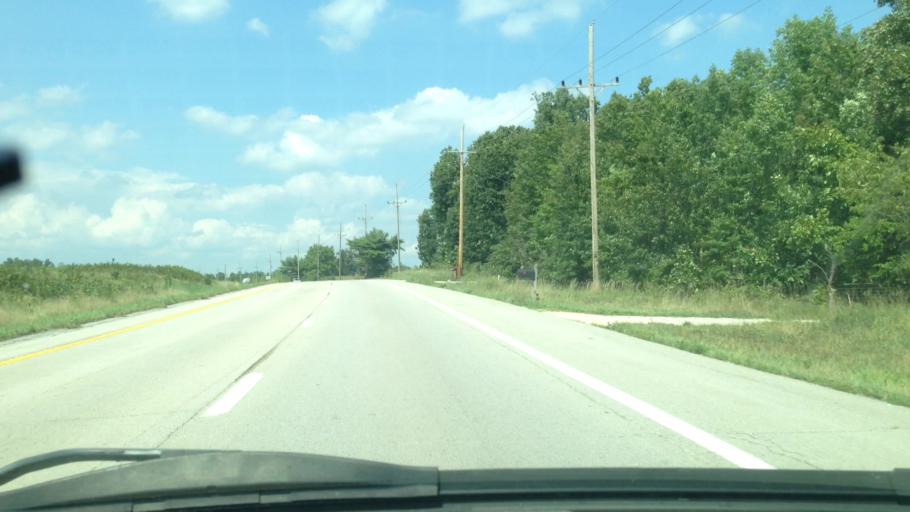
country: US
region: Missouri
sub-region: Lincoln County
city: Troy
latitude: 39.1122
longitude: -90.9597
